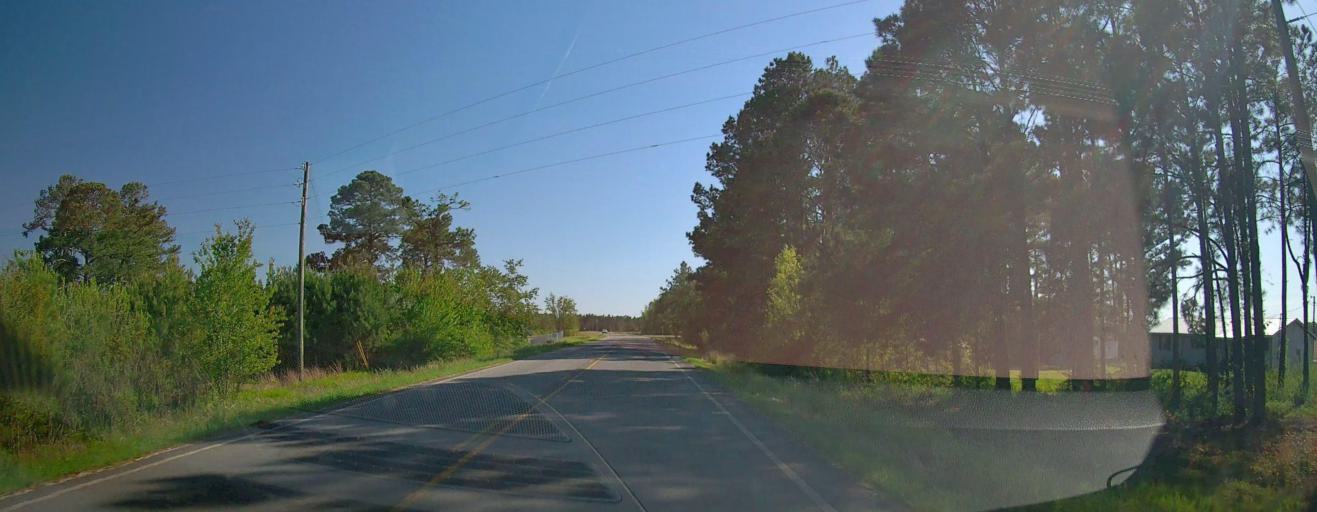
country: US
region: Georgia
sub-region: Wilcox County
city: Rochelle
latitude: 32.1021
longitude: -83.5021
